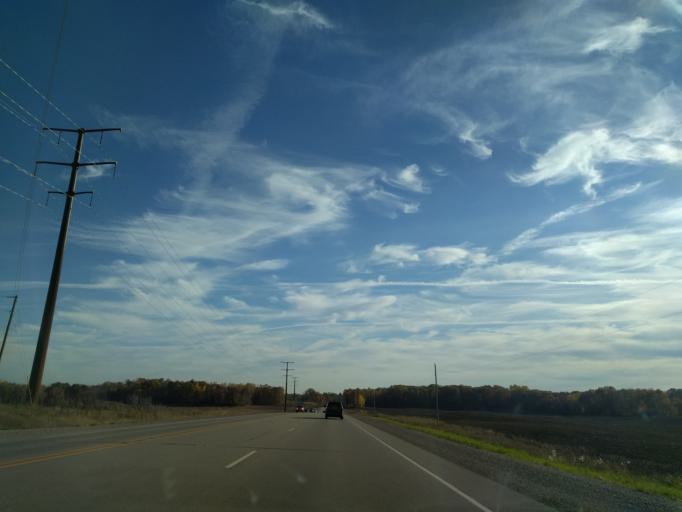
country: US
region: Wisconsin
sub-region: Marinette County
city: Peshtigo
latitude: 45.2674
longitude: -87.9906
